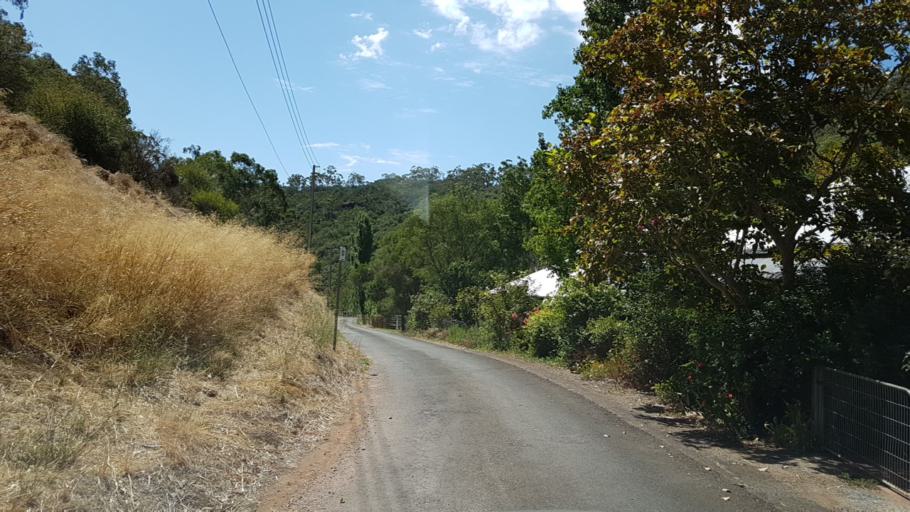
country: AU
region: South Australia
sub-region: Burnside
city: Mount Osmond
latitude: -34.9921
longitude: 138.6546
